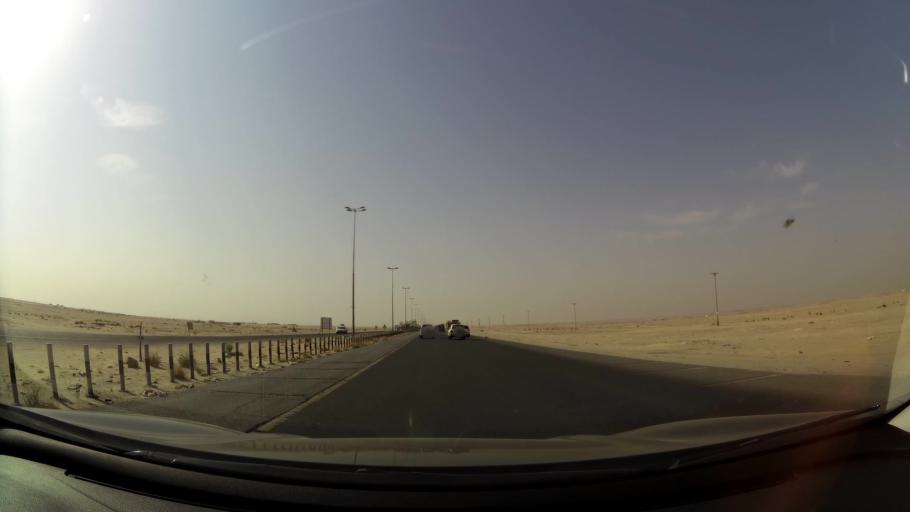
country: KW
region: Al Ahmadi
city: Al Ahmadi
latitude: 28.8804
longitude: 48.0800
